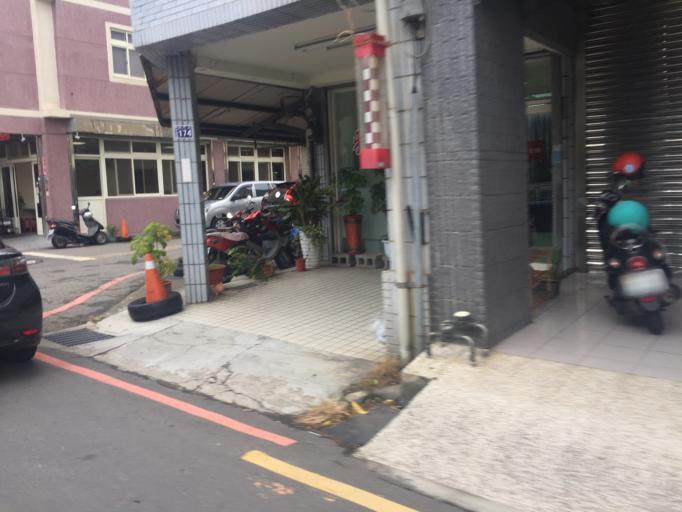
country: TW
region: Taiwan
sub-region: Hsinchu
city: Hsinchu
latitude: 24.8009
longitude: 120.9624
